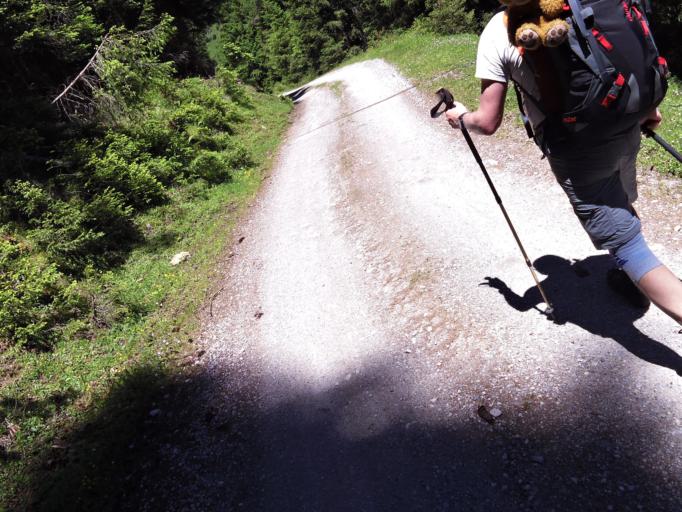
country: AT
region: Tyrol
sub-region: Politischer Bezirk Innsbruck Land
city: Neustift im Stubaital
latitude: 47.1160
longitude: 11.2932
